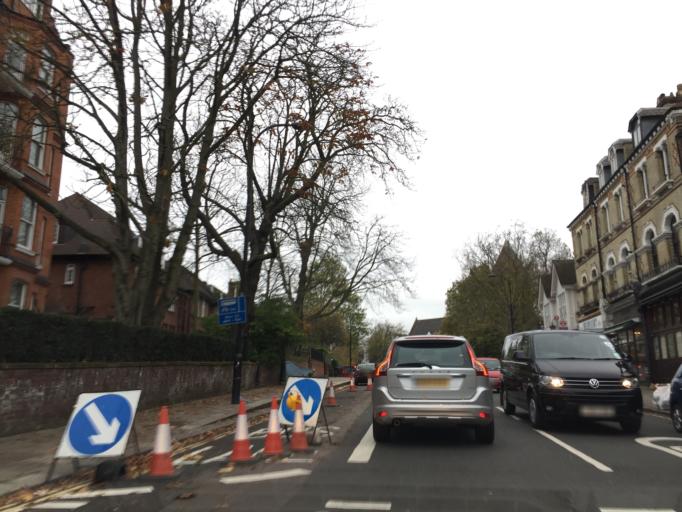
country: GB
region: England
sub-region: Greater London
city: Belsize Park
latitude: 51.5519
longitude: -0.1670
